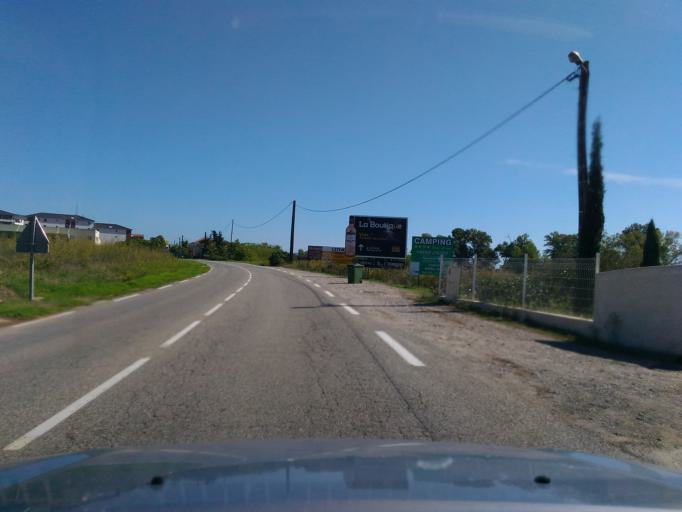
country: FR
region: Corsica
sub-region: Departement de la Haute-Corse
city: Aleria
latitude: 42.1127
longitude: 9.5083
